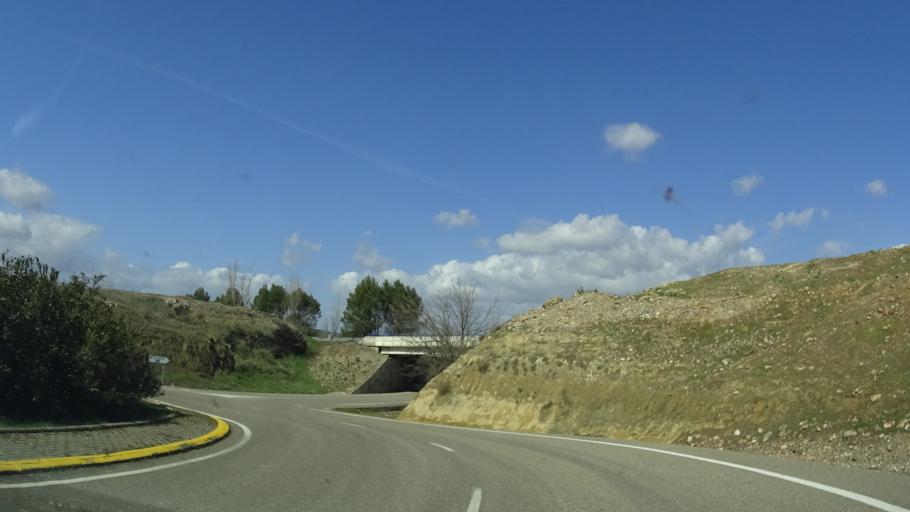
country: ES
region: Andalusia
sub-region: Province of Cordoba
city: Montoro
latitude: 38.0050
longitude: -4.3493
